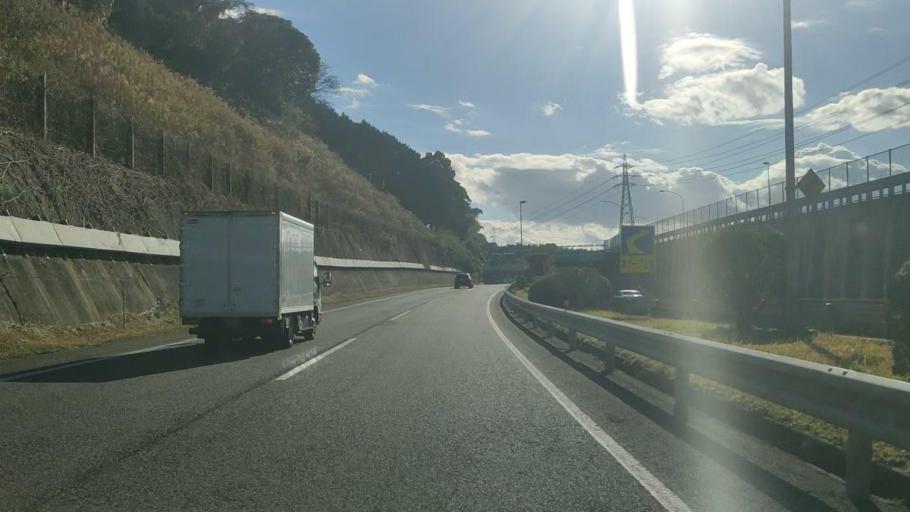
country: JP
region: Fukuoka
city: Kitakyushu
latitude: 33.8452
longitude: 130.7665
